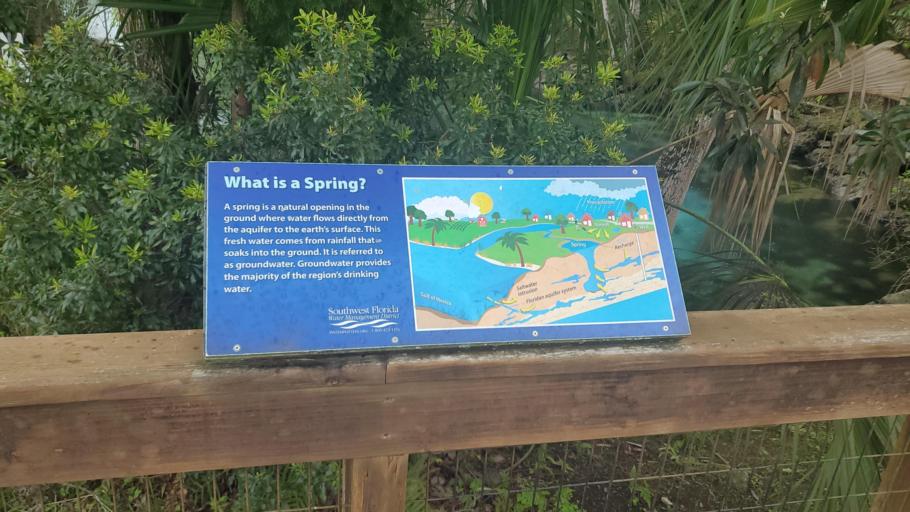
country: US
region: Florida
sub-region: Citrus County
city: Crystal River
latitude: 28.8890
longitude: -82.5897
